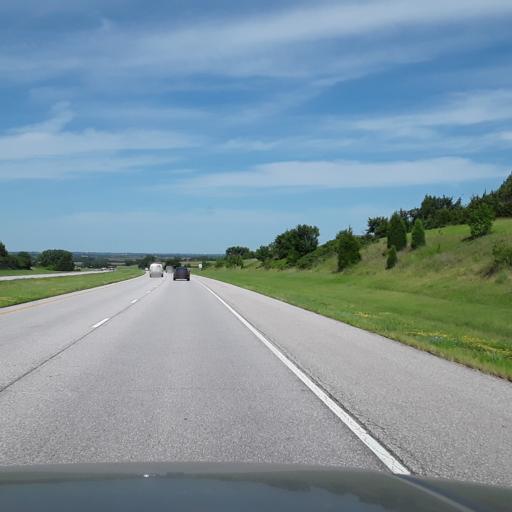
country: US
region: Nebraska
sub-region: Lancaster County
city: Lincoln
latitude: 40.8781
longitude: -96.7416
